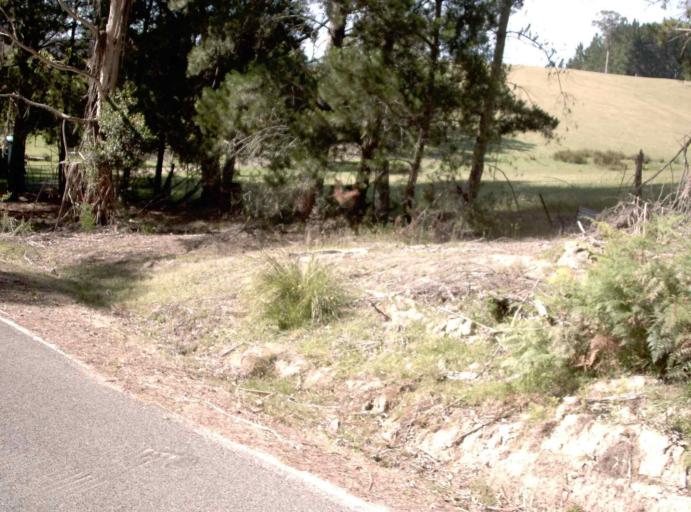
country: AU
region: New South Wales
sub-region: Bombala
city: Bombala
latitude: -37.3797
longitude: 148.6723
